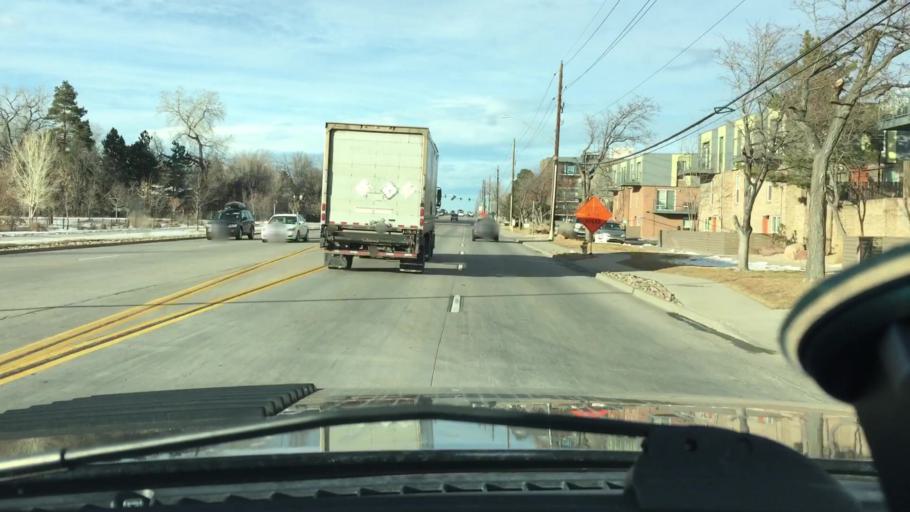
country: US
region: Colorado
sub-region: Adams County
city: Northglenn
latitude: 39.8897
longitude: -104.9966
